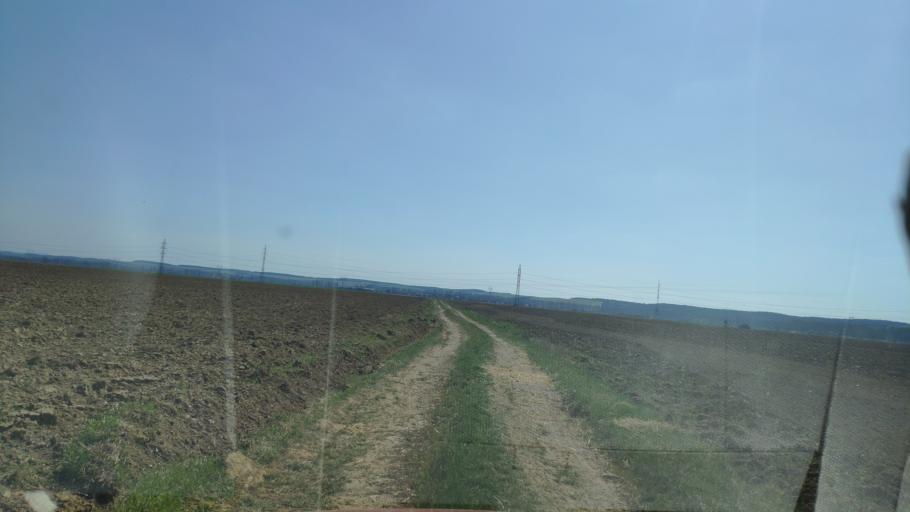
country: SK
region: Kosicky
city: Moldava nad Bodvou
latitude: 48.6027
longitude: 20.9441
